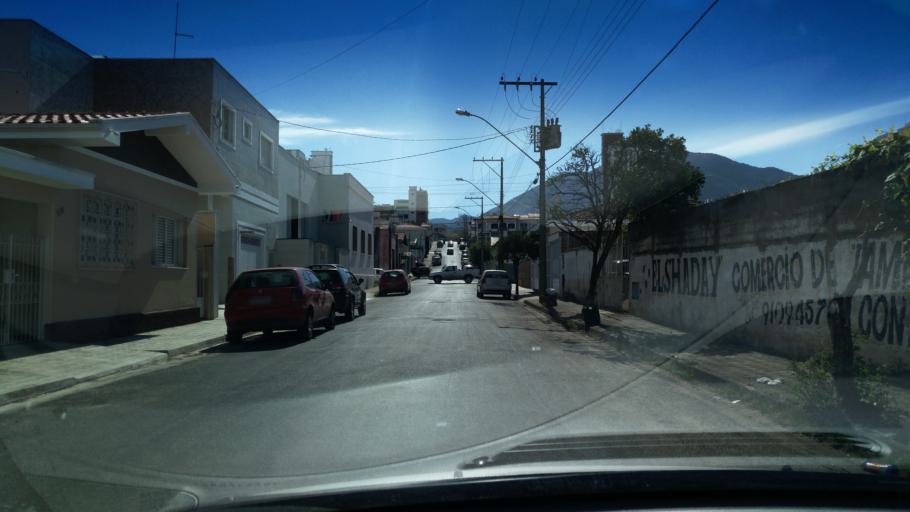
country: BR
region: Minas Gerais
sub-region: Andradas
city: Andradas
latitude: -22.0741
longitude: -46.5721
